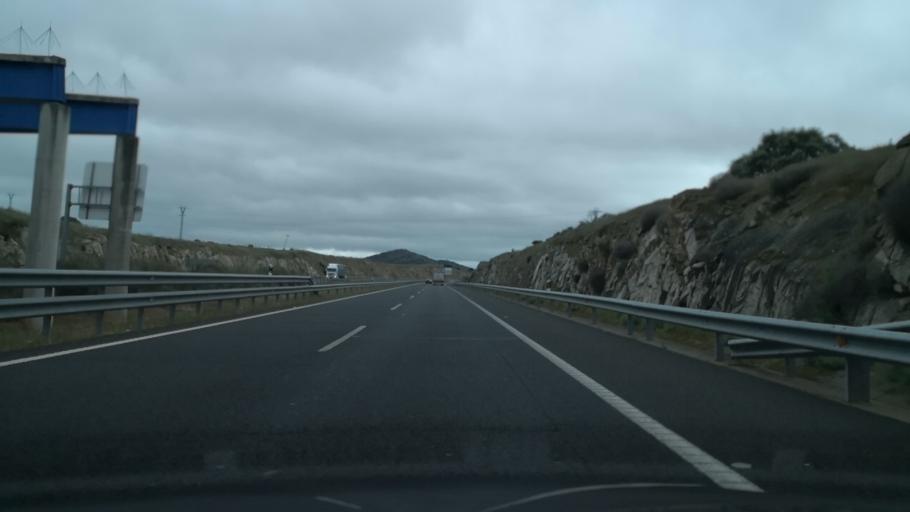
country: ES
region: Extremadura
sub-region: Provincia de Caceres
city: Caceres
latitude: 39.4531
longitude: -6.4172
